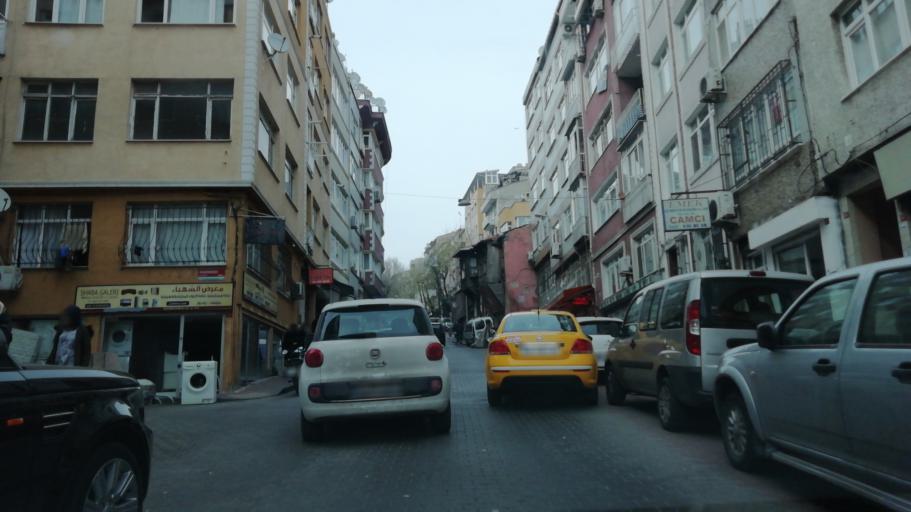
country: TR
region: Istanbul
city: Istanbul
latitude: 41.0140
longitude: 28.9487
